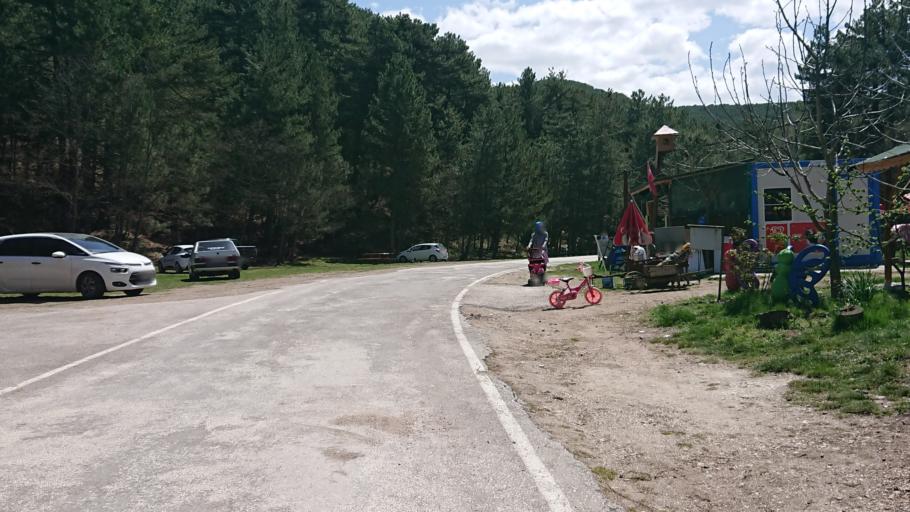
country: TR
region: Kuetahya
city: Sabuncu
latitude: 39.5140
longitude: 30.4242
